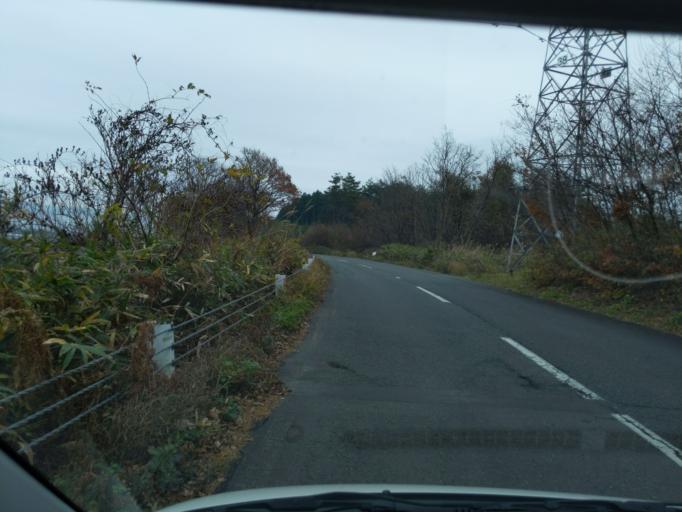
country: JP
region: Iwate
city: Mizusawa
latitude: 39.0447
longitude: 141.0826
